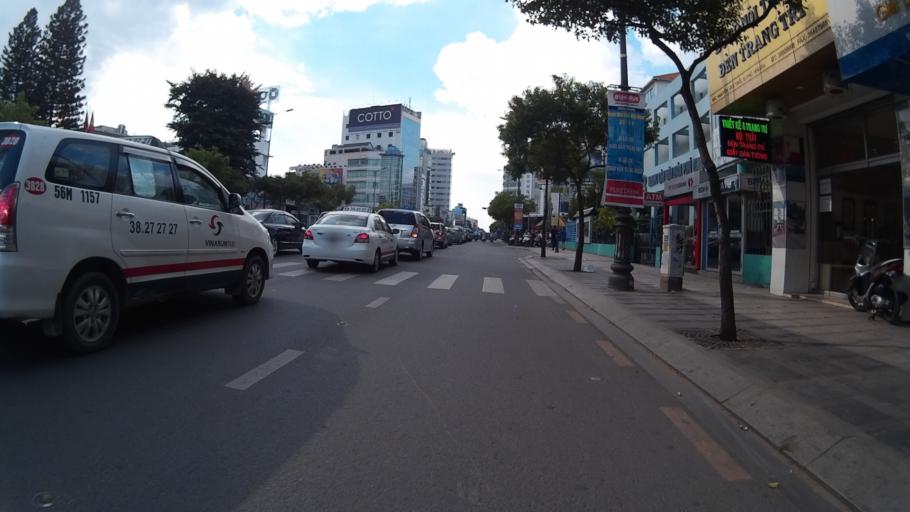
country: VN
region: Ho Chi Minh City
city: Quan Phu Nhuan
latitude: 10.7949
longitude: 106.6769
